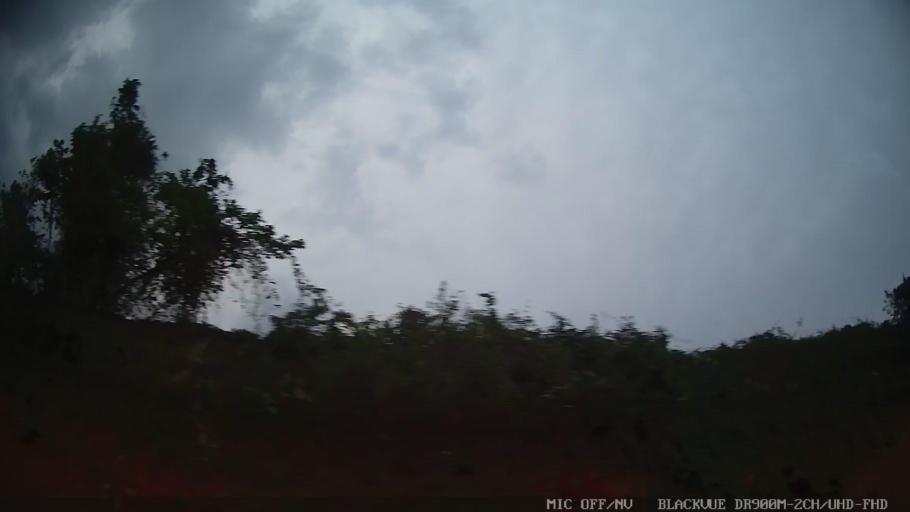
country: BR
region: Sao Paulo
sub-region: Braganca Paulista
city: Braganca Paulista
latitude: -22.9480
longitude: -46.5817
